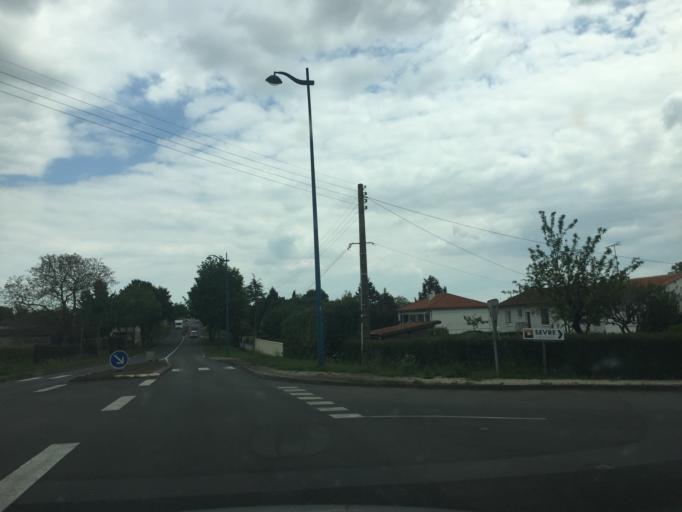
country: FR
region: Pays de la Loire
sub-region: Departement de la Vendee
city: Benet
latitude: 46.3751
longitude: -0.5900
